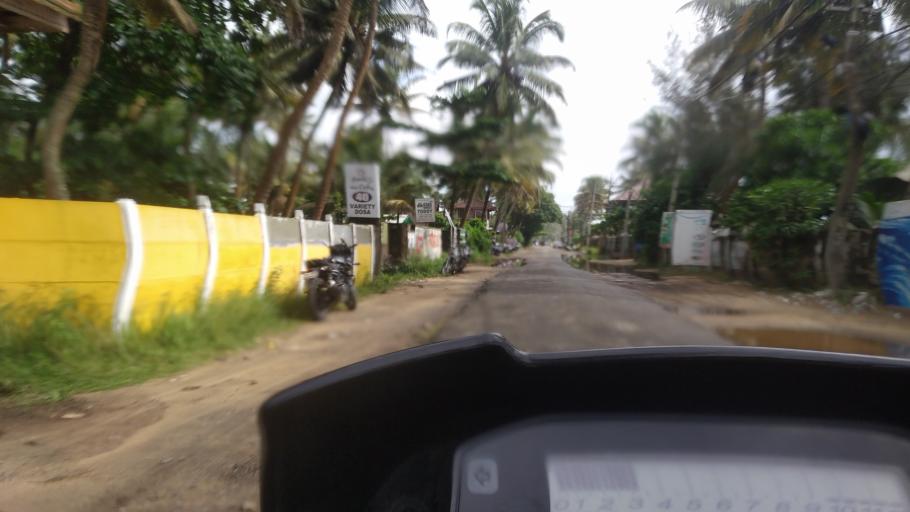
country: IN
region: Kerala
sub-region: Thrissur District
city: Kodungallur
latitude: 10.1425
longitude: 76.1784
